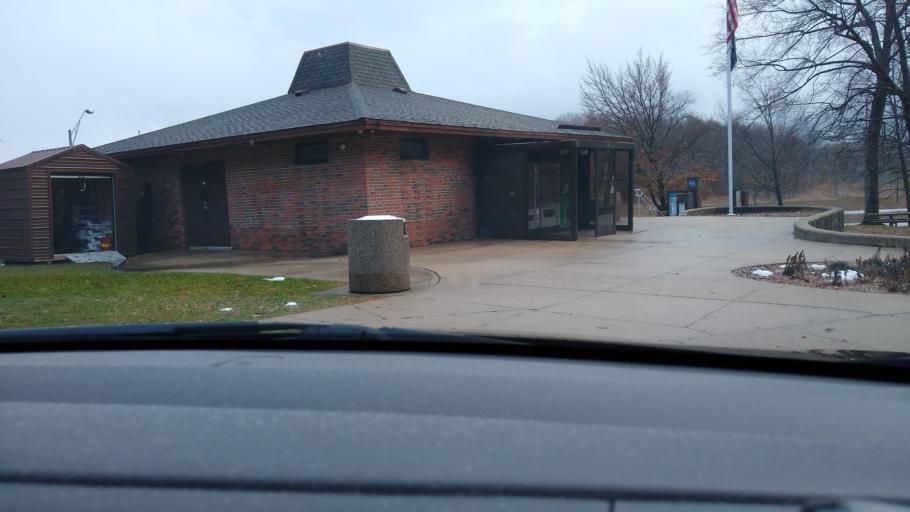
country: US
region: Michigan
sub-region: Otsego County
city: Gaylord
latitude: 45.1066
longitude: -84.6893
